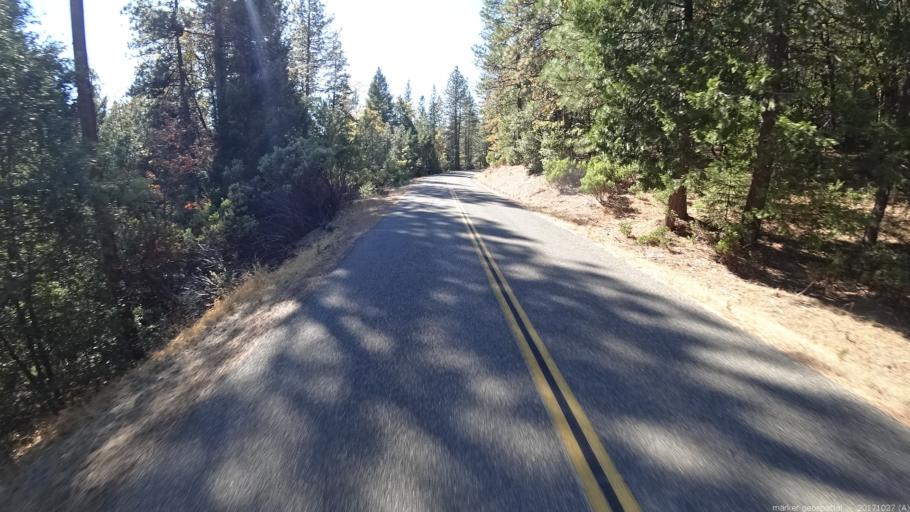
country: US
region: California
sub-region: Shasta County
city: Shingletown
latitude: 40.6885
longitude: -121.9273
